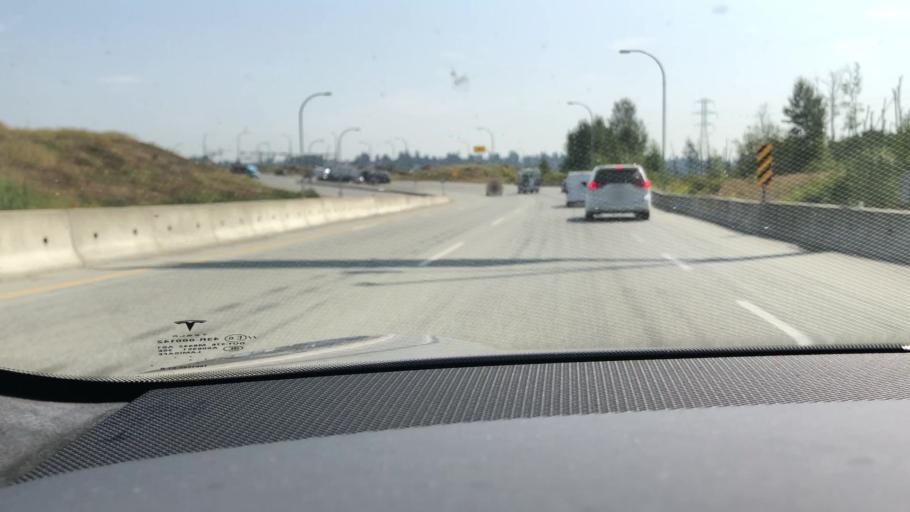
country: CA
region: British Columbia
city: Delta
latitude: 49.1484
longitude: -122.9570
